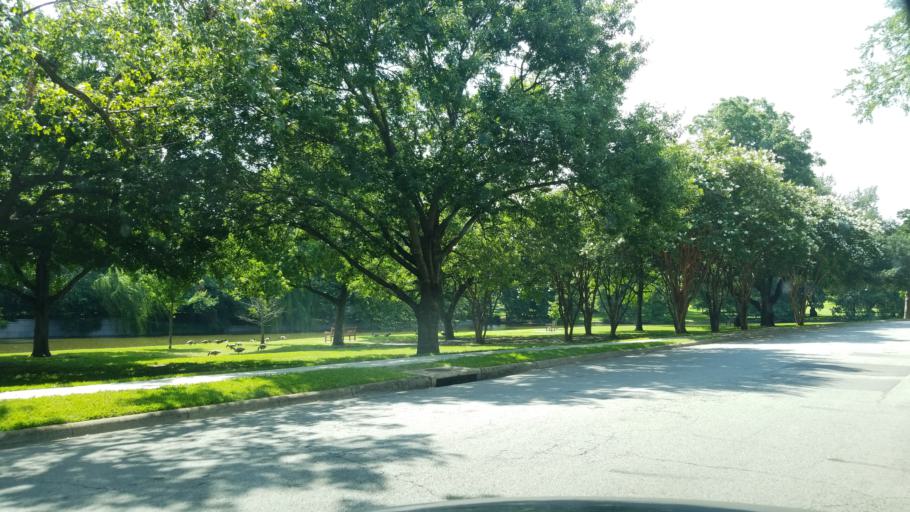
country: US
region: Texas
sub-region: Dallas County
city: Highland Park
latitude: 32.8280
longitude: -96.8014
